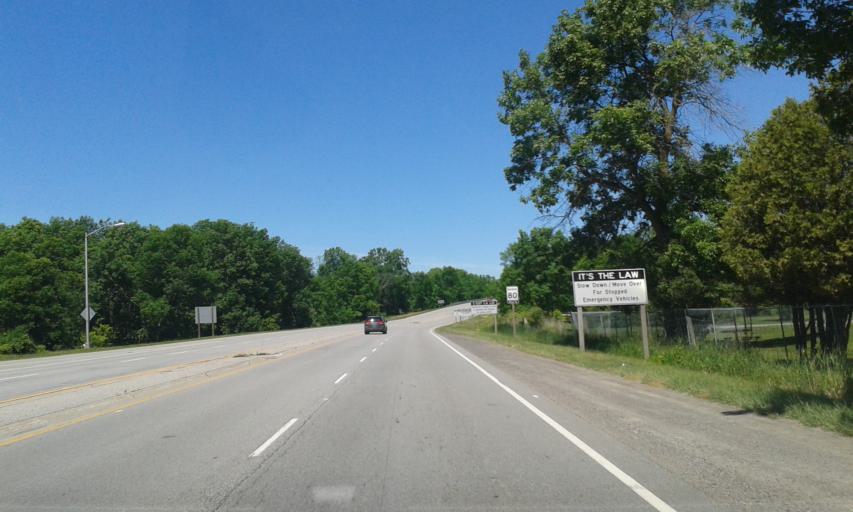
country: CA
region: Ontario
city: Prescott
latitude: 44.7480
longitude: -75.4718
